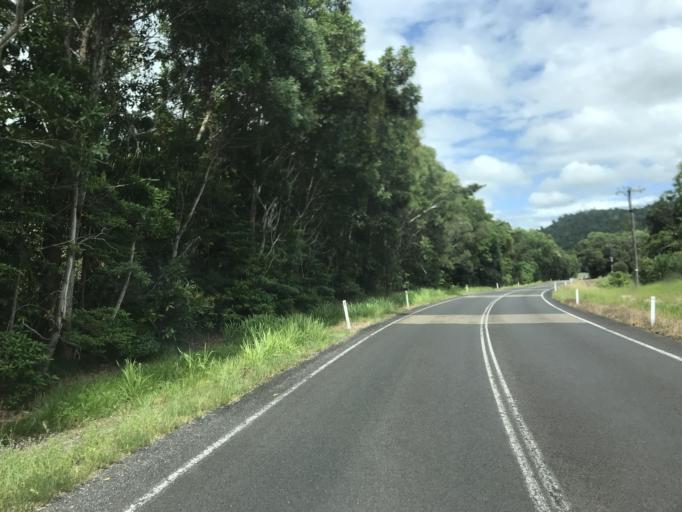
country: AU
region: Queensland
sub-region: Cassowary Coast
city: Innisfail
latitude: -17.8696
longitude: 146.0853
